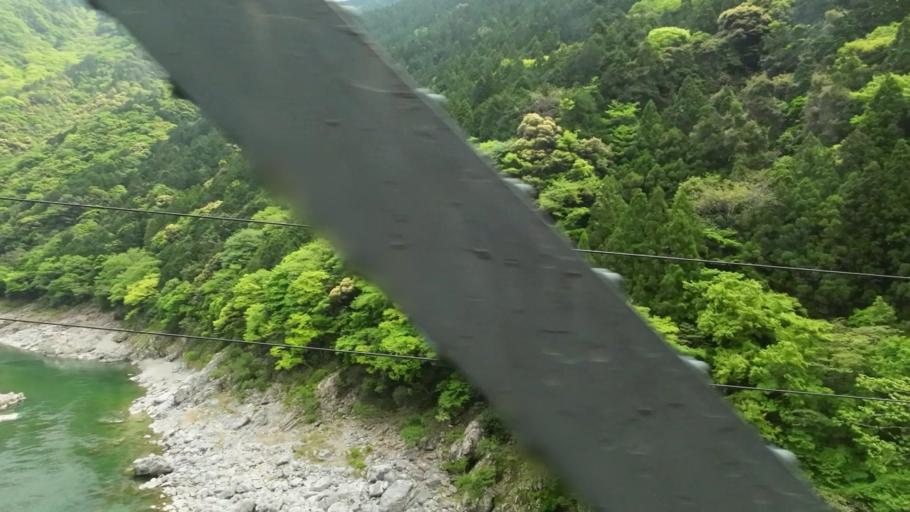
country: JP
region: Tokushima
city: Ikedacho
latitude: 33.9105
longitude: 133.7574
